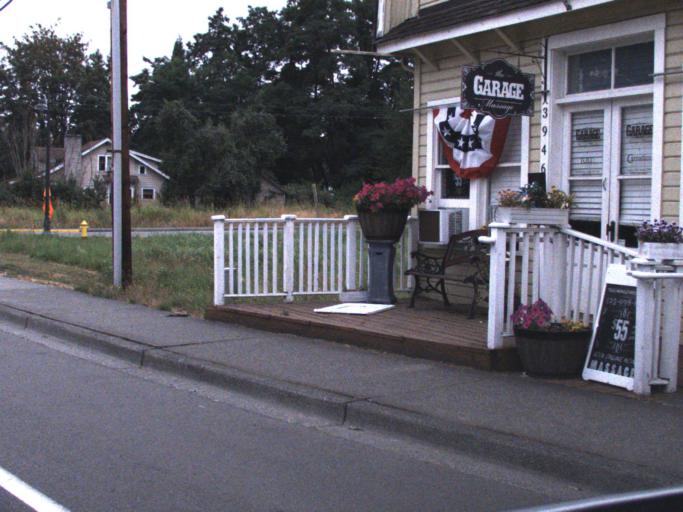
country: US
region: Washington
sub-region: King County
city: Carnation
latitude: 47.6443
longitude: -121.9156
